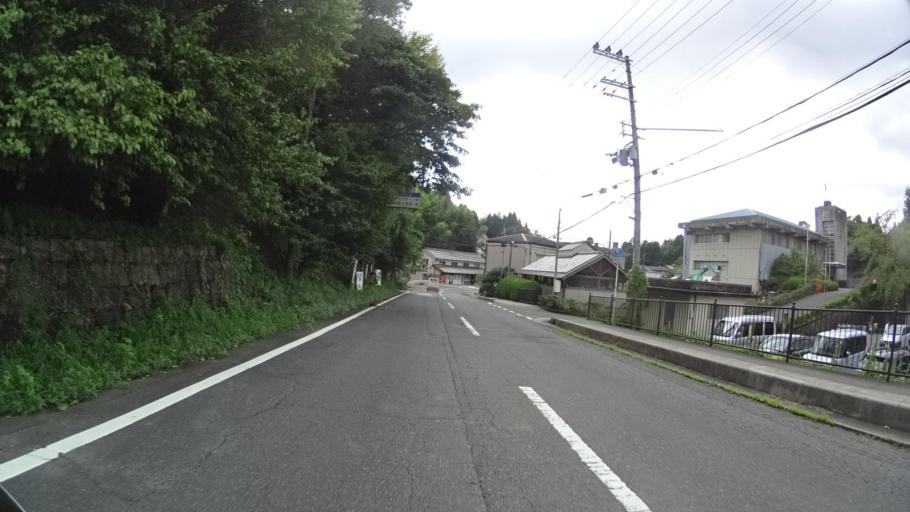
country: JP
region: Mie
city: Ueno-ebisumachi
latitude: 34.7099
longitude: 136.0449
